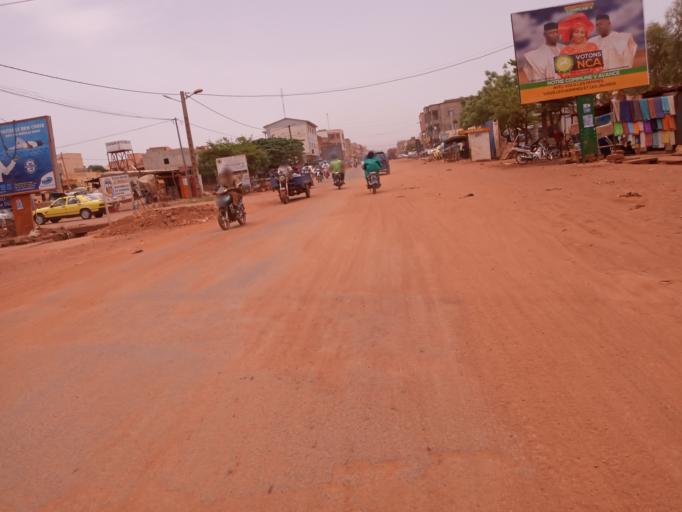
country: ML
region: Bamako
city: Bamako
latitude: 12.5819
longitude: -8.0205
